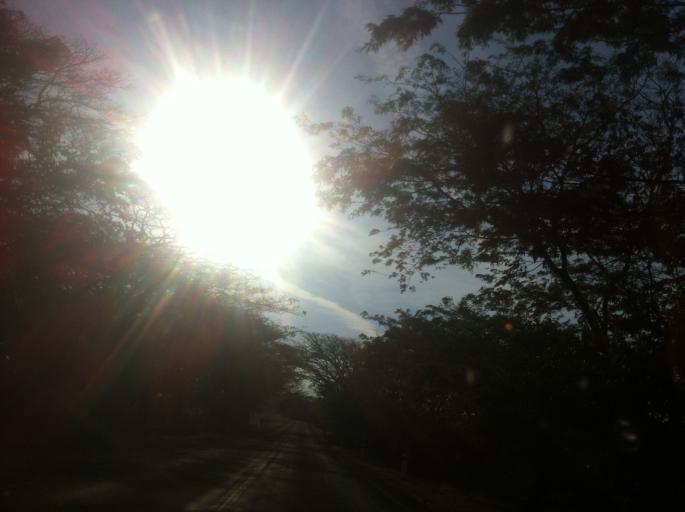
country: NI
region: Rivas
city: Cardenas
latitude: 11.2737
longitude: -85.6531
